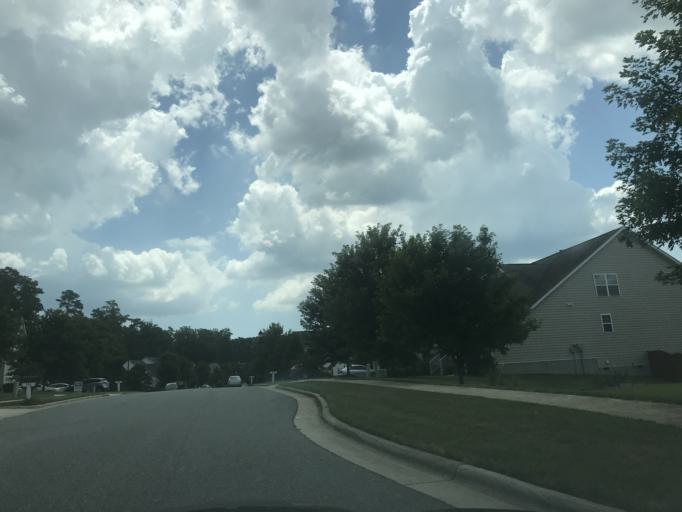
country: US
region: North Carolina
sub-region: Wake County
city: Wake Forest
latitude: 35.9608
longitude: -78.5280
